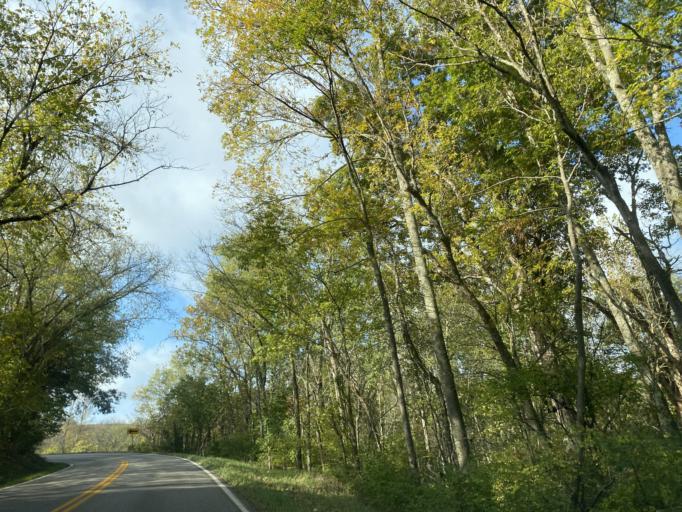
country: US
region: Kentucky
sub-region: Pendleton County
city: Falmouth
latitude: 38.7131
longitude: -84.3030
